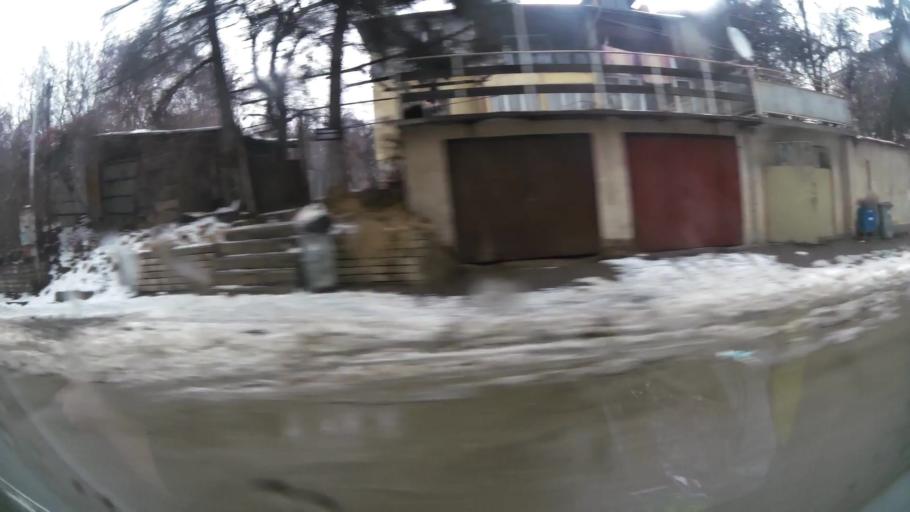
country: BG
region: Sofia-Capital
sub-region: Stolichna Obshtina
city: Sofia
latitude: 42.6737
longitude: 23.2536
